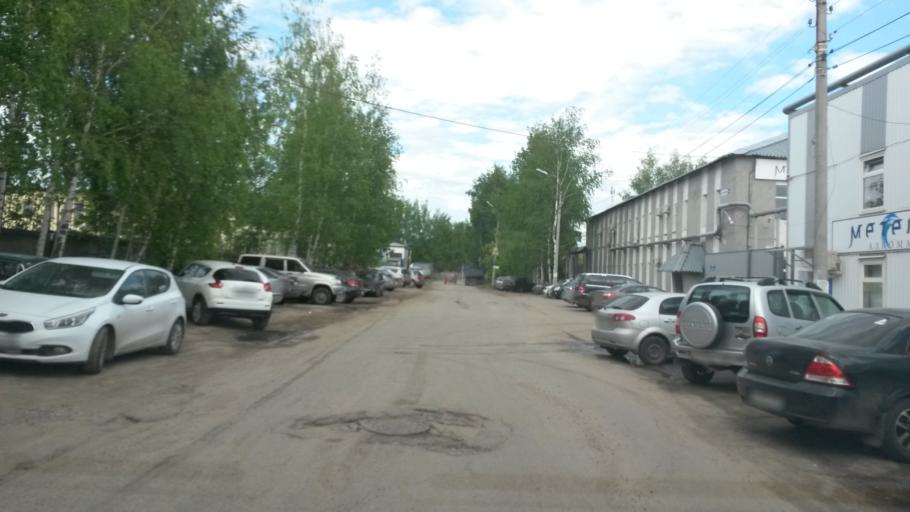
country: RU
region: Jaroslavl
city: Yaroslavl
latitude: 57.6488
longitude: 39.9106
